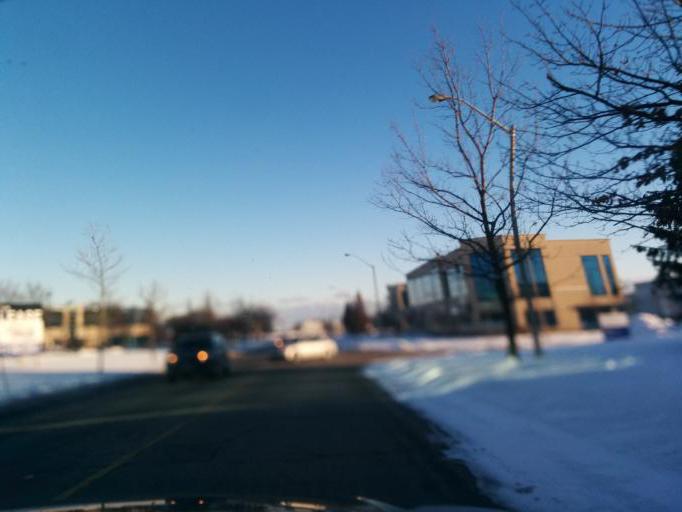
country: CA
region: Ontario
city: Mississauga
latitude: 43.5192
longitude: -79.6792
